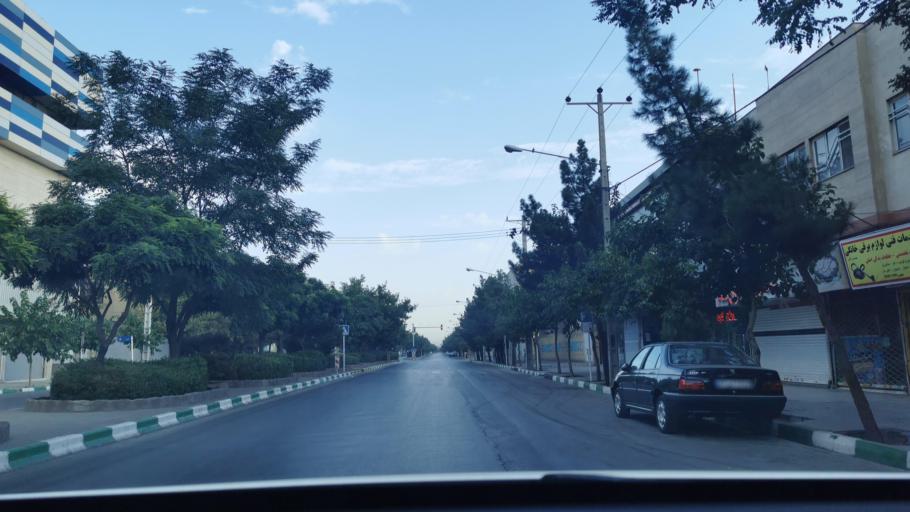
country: IR
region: Razavi Khorasan
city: Mashhad
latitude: 36.3571
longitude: 59.5255
